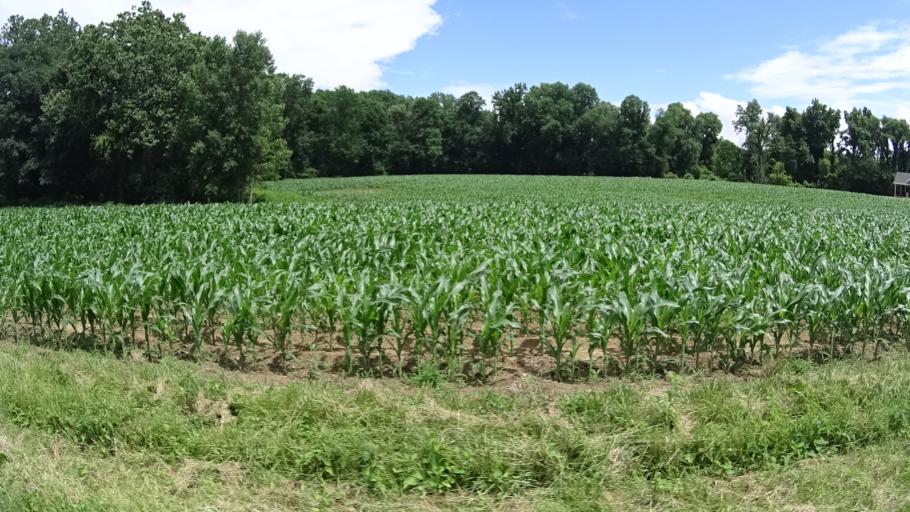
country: US
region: Ohio
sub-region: Erie County
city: Milan
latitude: 41.2871
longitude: -82.6227
